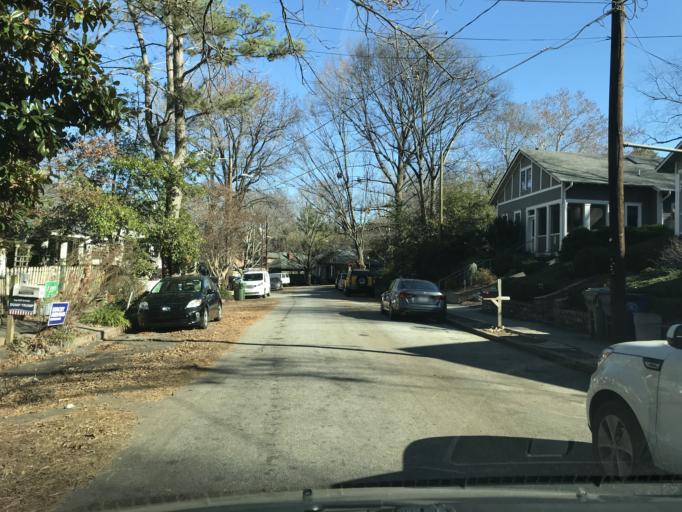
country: US
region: Georgia
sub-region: Fulton County
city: Atlanta
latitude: 33.7587
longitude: -84.3601
